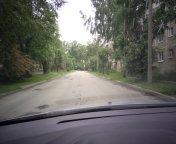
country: RU
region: Sverdlovsk
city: Sovkhoznyy
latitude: 56.7648
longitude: 60.6117
